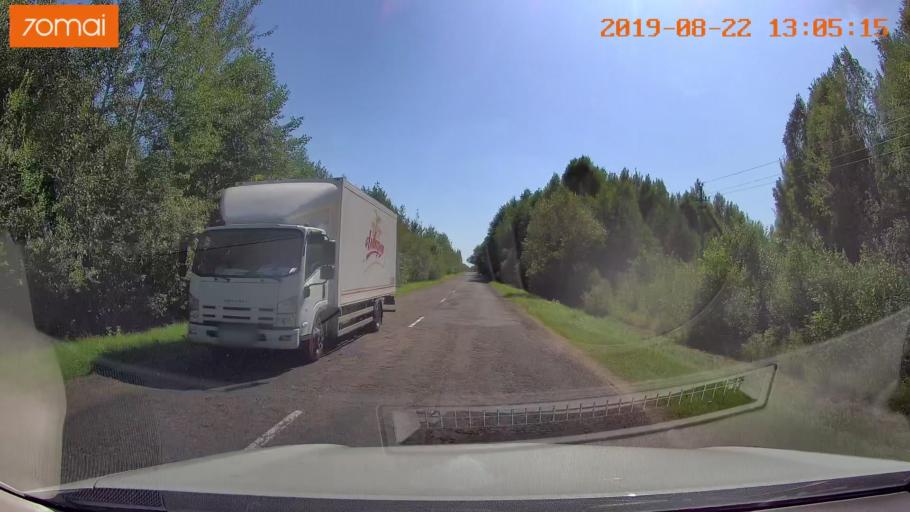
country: BY
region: Minsk
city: Prawdzinski
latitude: 53.3615
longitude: 27.8330
